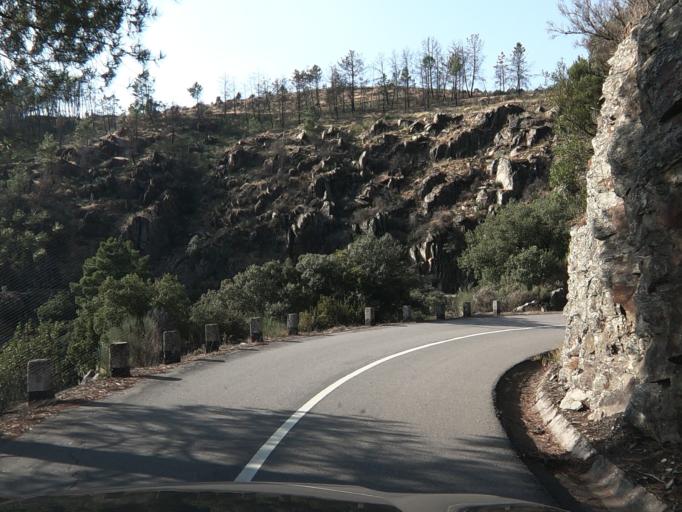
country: PT
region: Vila Real
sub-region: Sabrosa
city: Vilela
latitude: 41.2138
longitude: -7.6148
